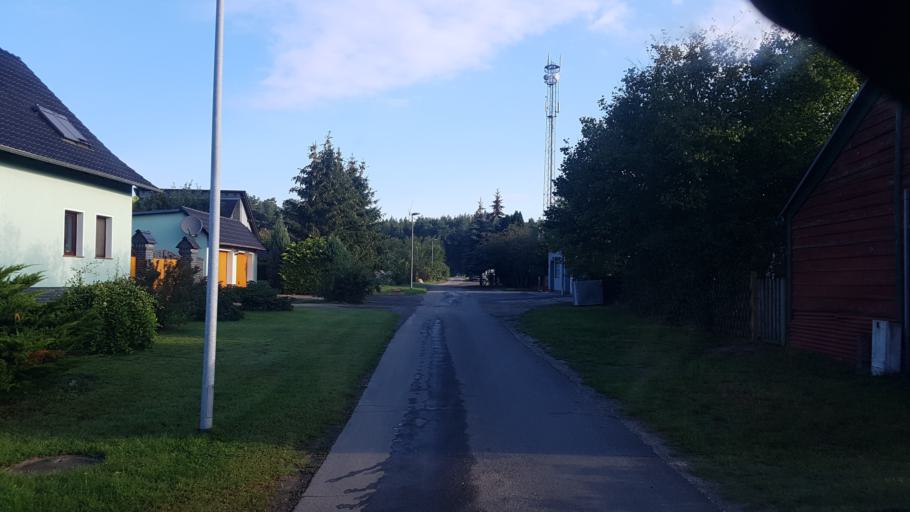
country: DE
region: Brandenburg
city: Bronkow
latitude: 51.6746
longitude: 13.8919
